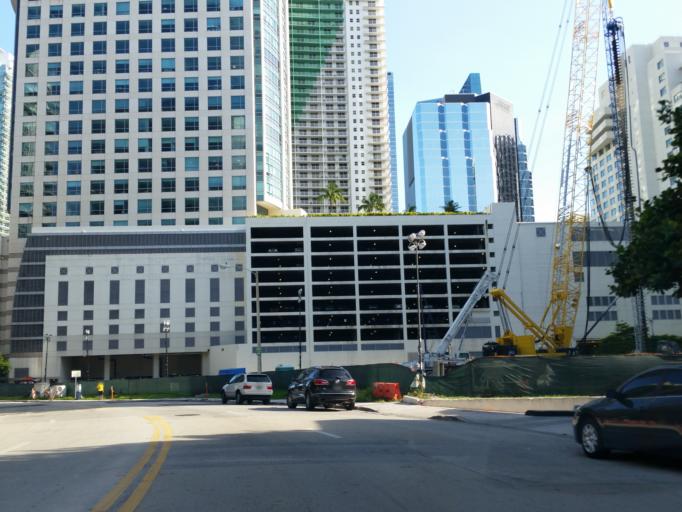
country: US
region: Florida
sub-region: Miami-Dade County
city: Miami
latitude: 25.7637
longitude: -80.1901
